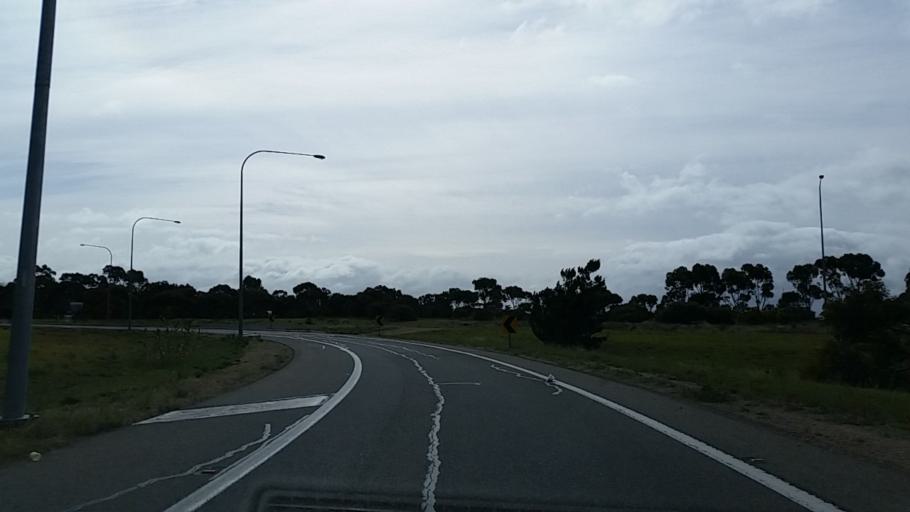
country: AU
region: South Australia
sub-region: Murray Bridge
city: Murray Bridge
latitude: -35.1501
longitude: 139.2885
